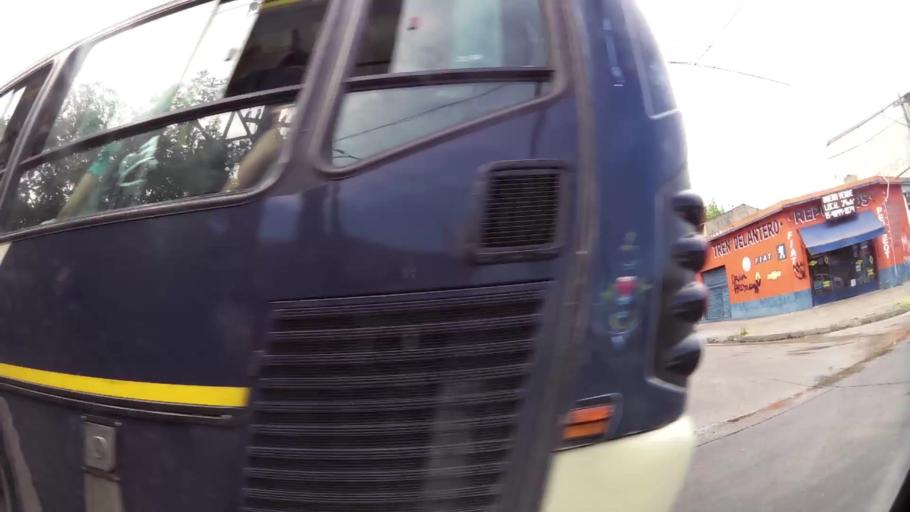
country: AR
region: Buenos Aires
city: Ituzaingo
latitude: -34.6466
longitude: -58.6806
